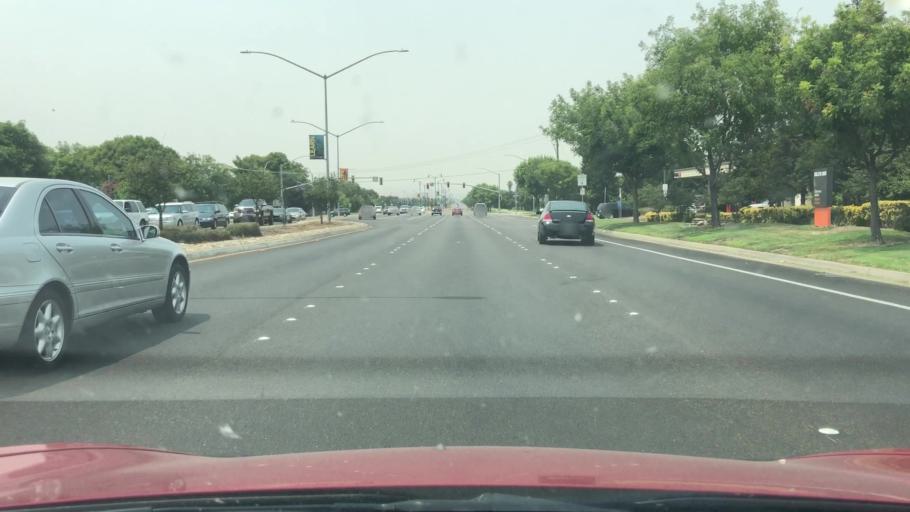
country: US
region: California
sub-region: San Joaquin County
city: Tracy
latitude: 37.7394
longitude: -121.4512
